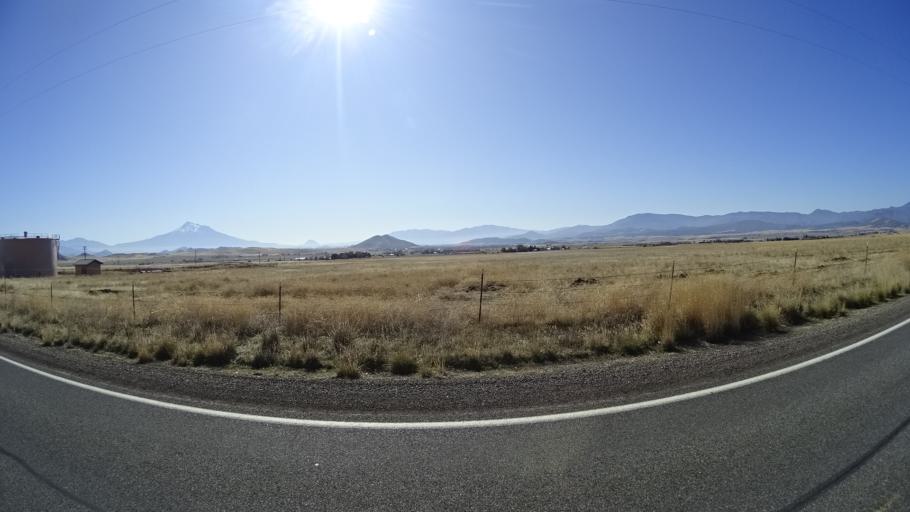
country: US
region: California
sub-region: Siskiyou County
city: Montague
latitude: 41.7716
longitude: -122.5265
